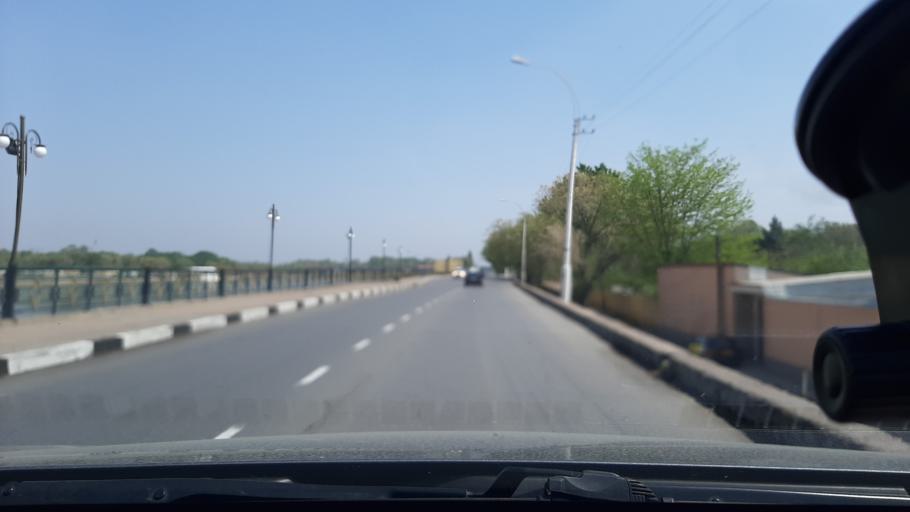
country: TJ
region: Viloyati Sughd
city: Khujand
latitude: 40.2926
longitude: 69.6315
